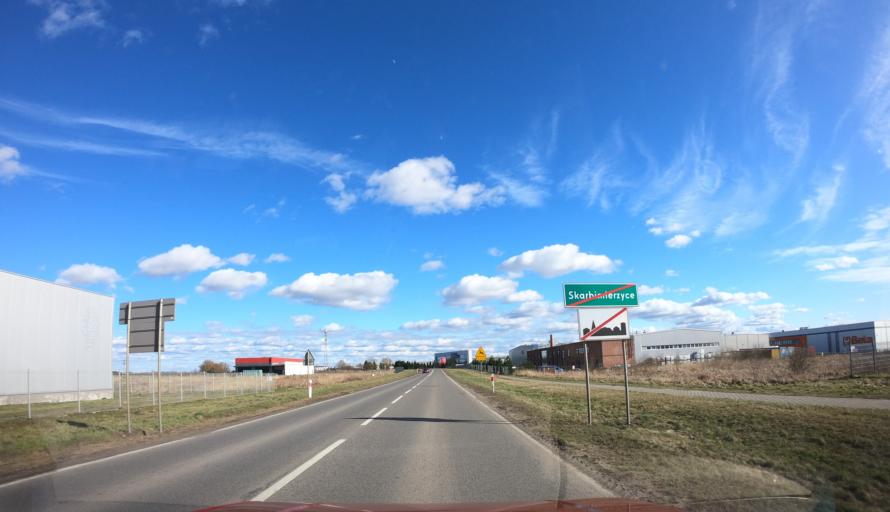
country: PL
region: West Pomeranian Voivodeship
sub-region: Powiat policki
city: Dobra
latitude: 53.4339
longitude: 14.4310
